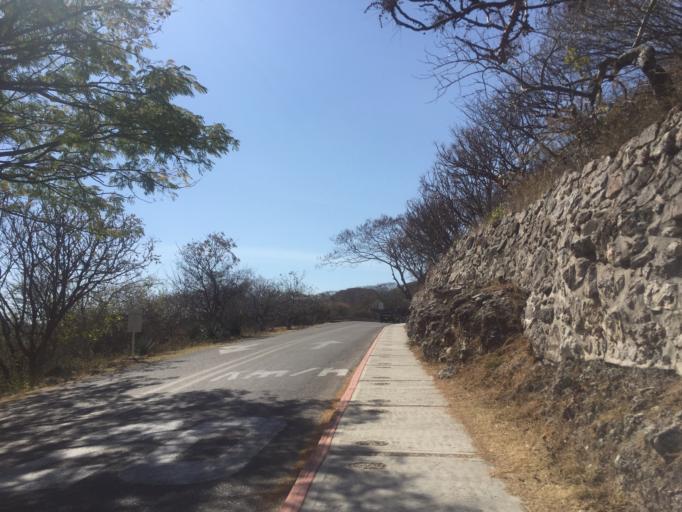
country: MX
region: Morelos
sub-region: Miacatlan
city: Xochicalco (Cirenio Longares)
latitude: 18.8042
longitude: -99.2930
